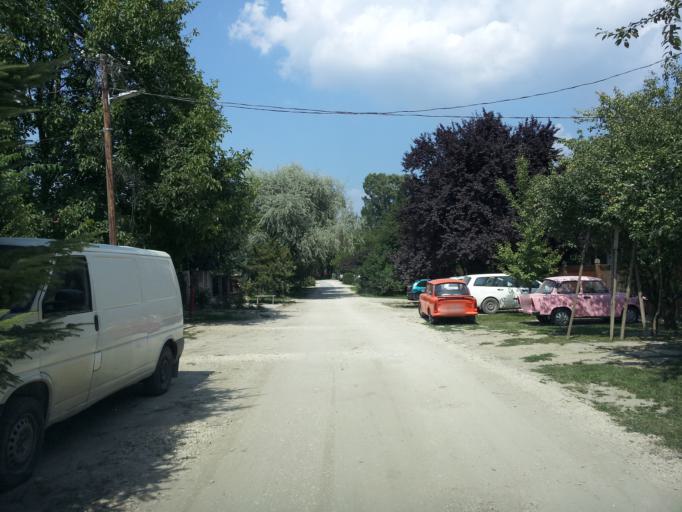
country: HU
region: Pest
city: Szigetszentmiklos
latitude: 47.3364
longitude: 19.0507
